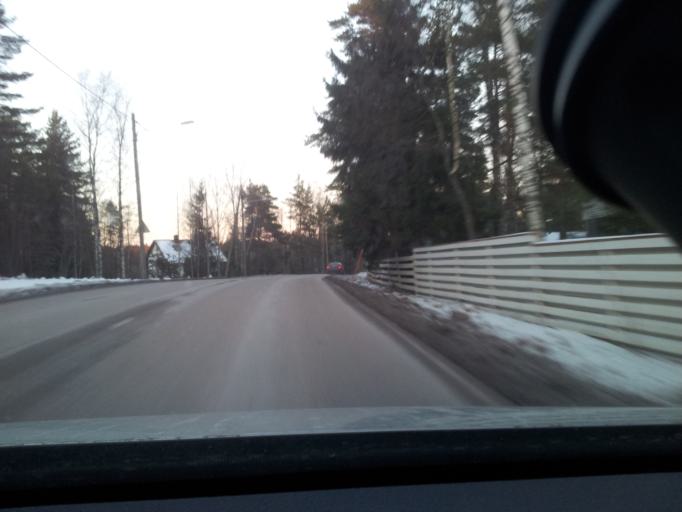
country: FI
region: Uusimaa
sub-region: Helsinki
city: Espoo
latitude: 60.1486
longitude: 24.6837
